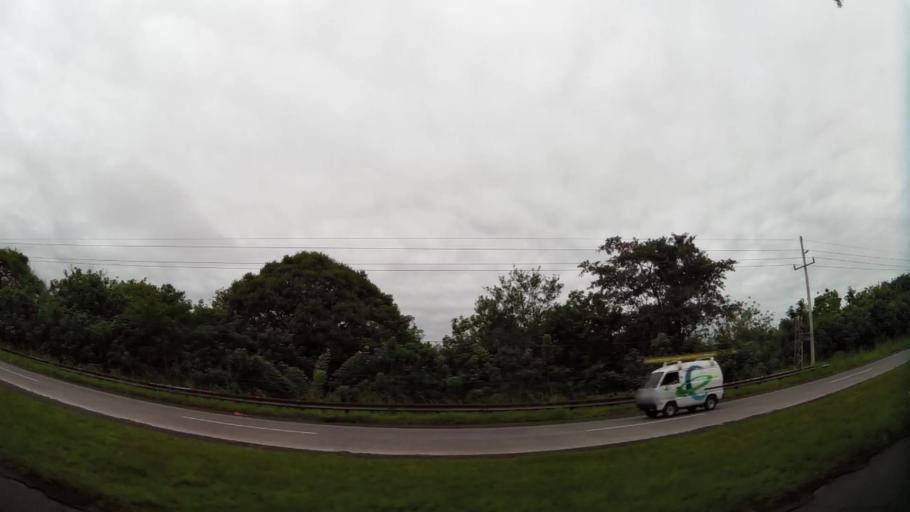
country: PA
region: Chiriqui
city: Boqueron
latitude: 8.4870
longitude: -82.5698
